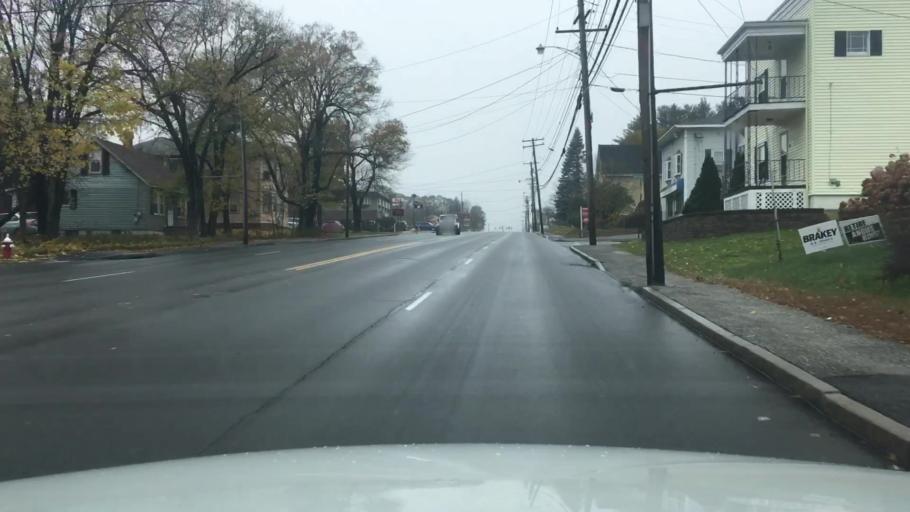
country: US
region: Maine
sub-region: Androscoggin County
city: Lewiston
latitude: 44.1025
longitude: -70.1683
